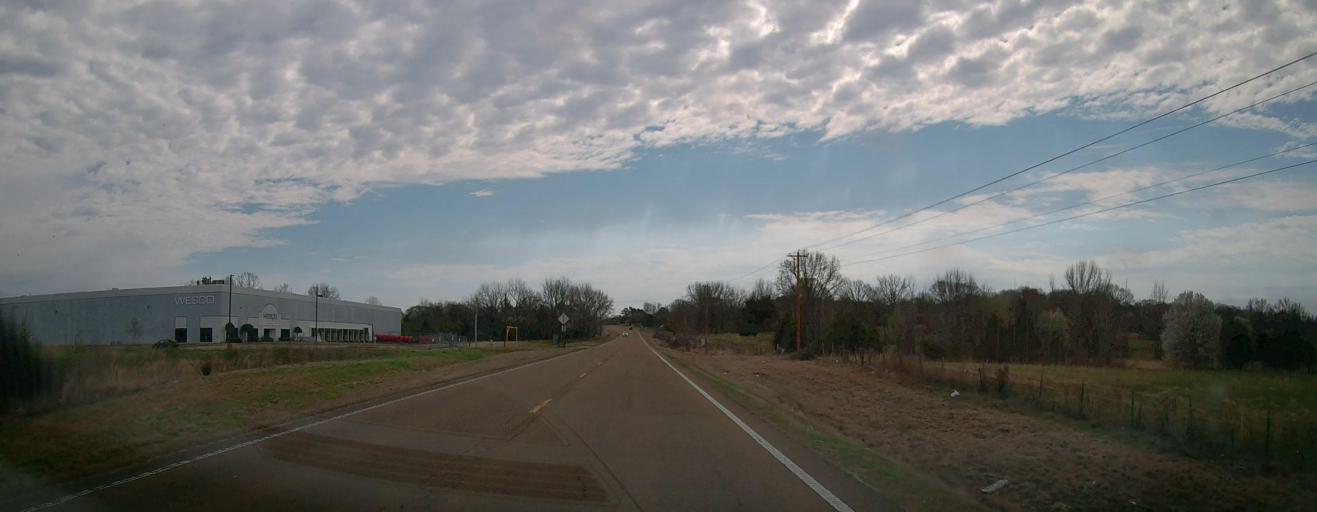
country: US
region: Mississippi
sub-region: Marshall County
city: Byhalia
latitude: 34.8646
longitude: -89.6616
